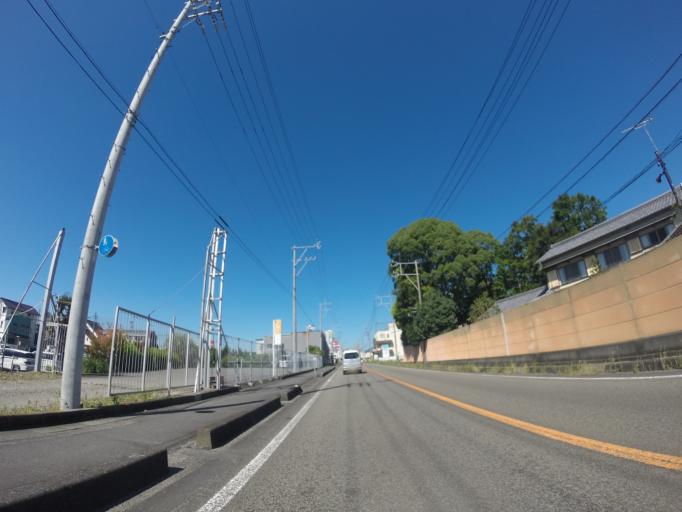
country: JP
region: Shizuoka
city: Shimada
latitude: 34.8361
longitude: 138.1869
